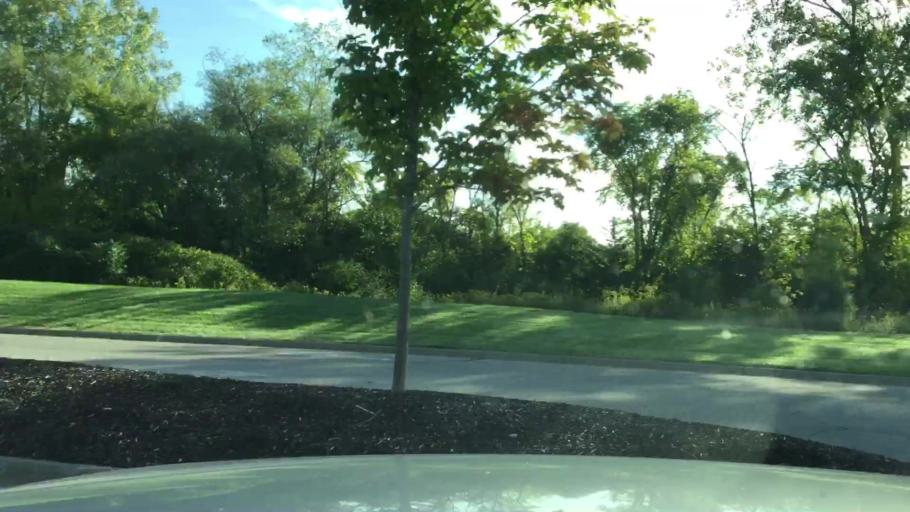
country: US
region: Michigan
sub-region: Genesee County
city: Flushing
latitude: 43.0615
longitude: -83.7833
